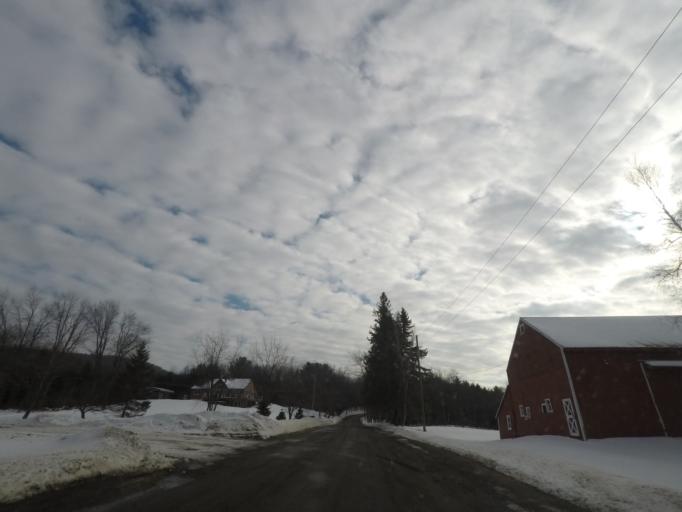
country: US
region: New York
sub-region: Rensselaer County
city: Averill Park
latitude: 42.6415
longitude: -73.4800
